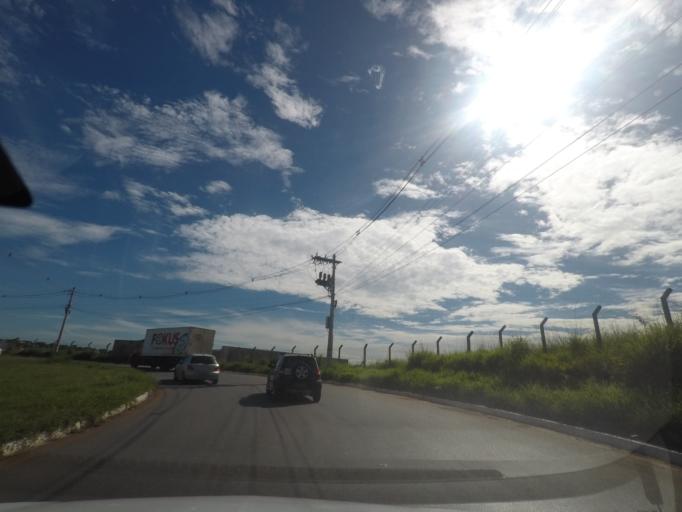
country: BR
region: Goias
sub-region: Aparecida De Goiania
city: Aparecida de Goiania
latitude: -16.7854
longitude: -49.2508
